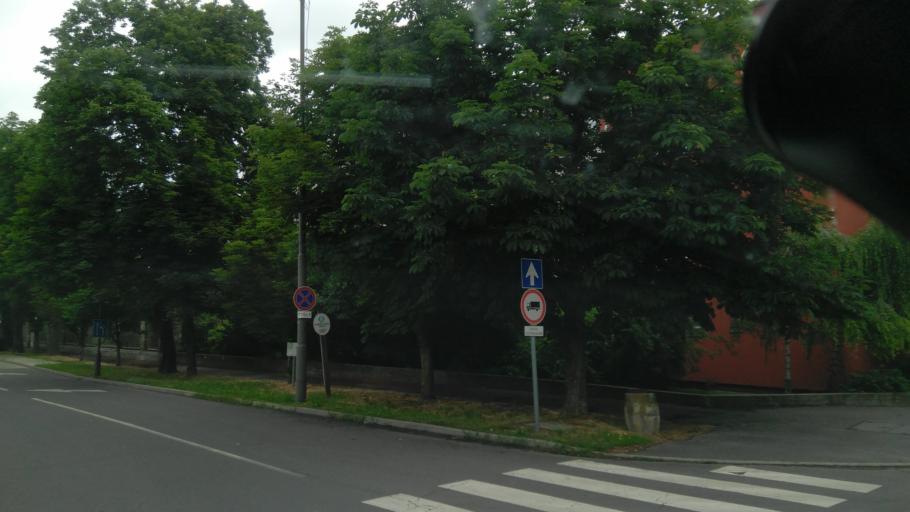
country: HU
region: Bekes
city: Bekescsaba
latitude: 46.6777
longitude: 21.1024
